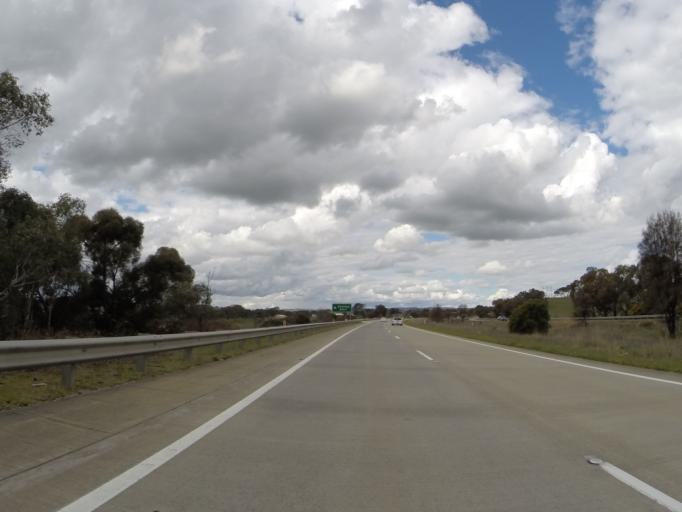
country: AU
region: New South Wales
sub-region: Yass Valley
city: Gundaroo
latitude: -34.7850
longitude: 149.2487
